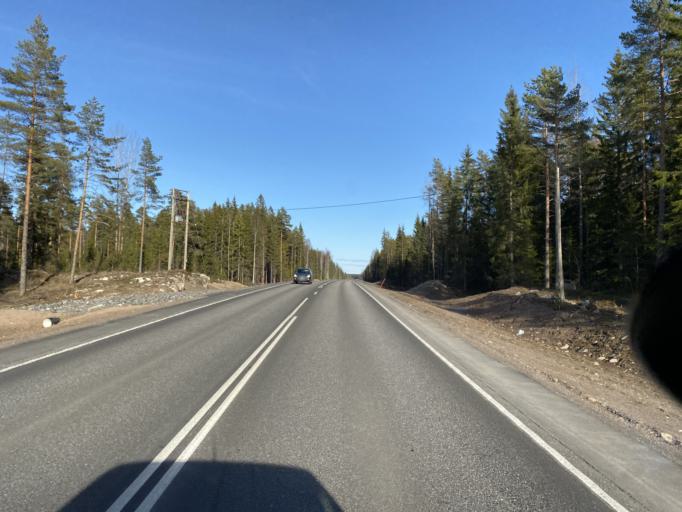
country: FI
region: Satakunta
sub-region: Pori
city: Kokemaeki
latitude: 61.1730
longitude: 22.5175
